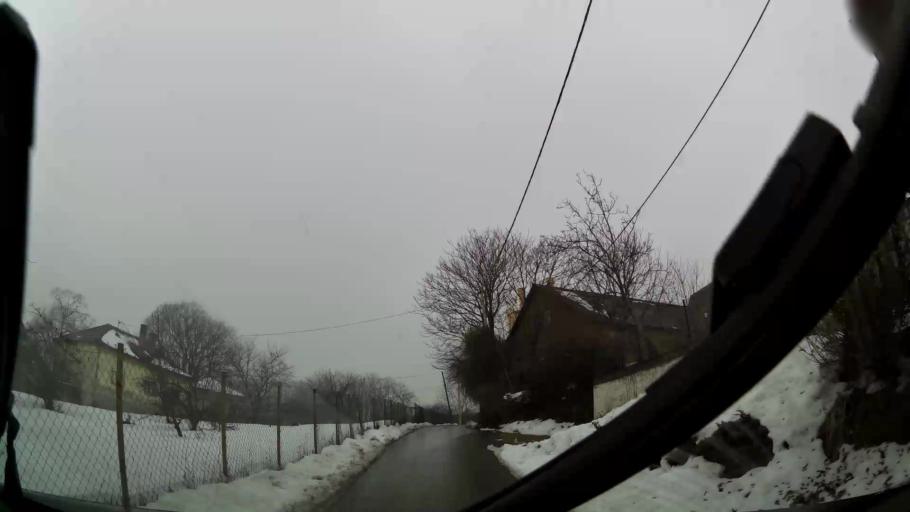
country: RS
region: Central Serbia
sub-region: Belgrade
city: Zvezdara
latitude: 44.7783
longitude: 20.5249
